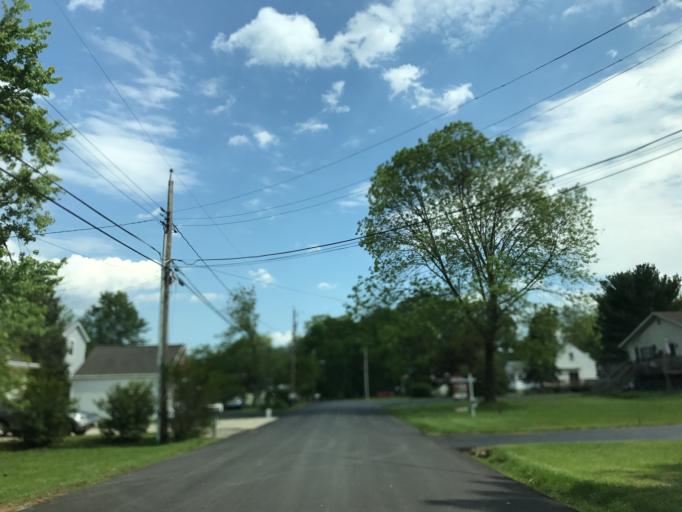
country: US
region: Maryland
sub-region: Baltimore County
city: Bowleys Quarters
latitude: 39.3754
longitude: -76.3519
